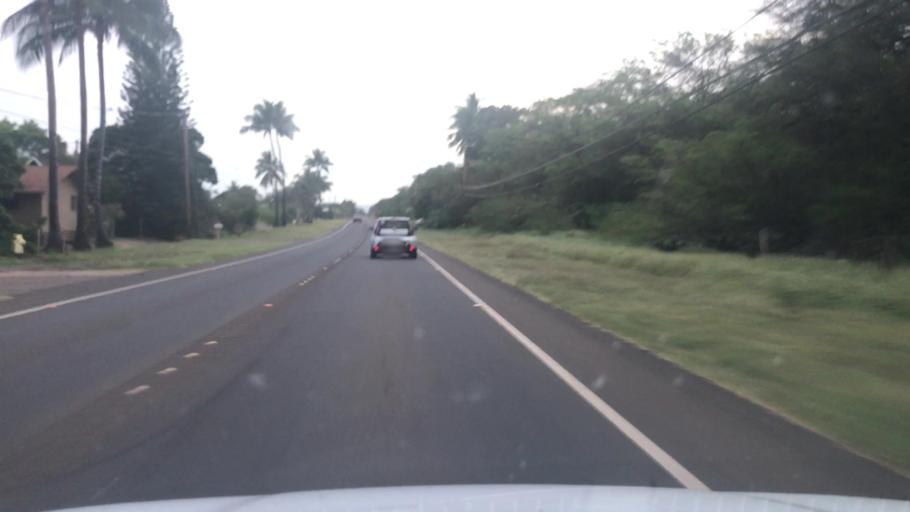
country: US
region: Hawaii
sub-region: Maui County
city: Kaunakakai
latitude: 21.0691
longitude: -156.9623
